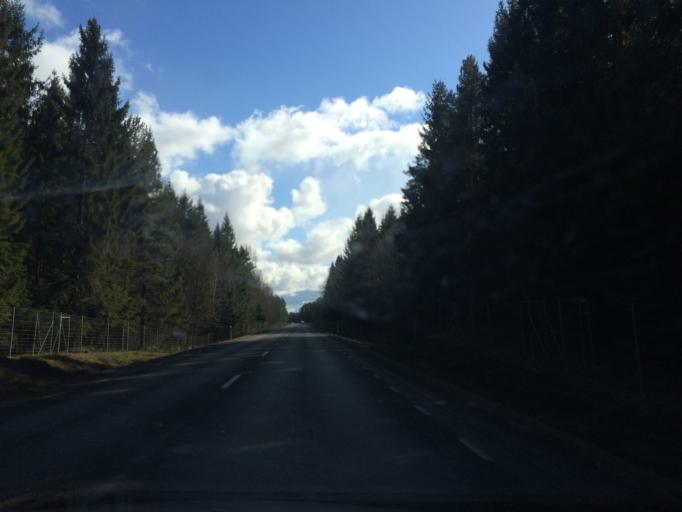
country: SE
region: Vaestra Goetaland
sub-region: Skara Kommun
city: Skara
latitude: 58.3678
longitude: 13.4183
